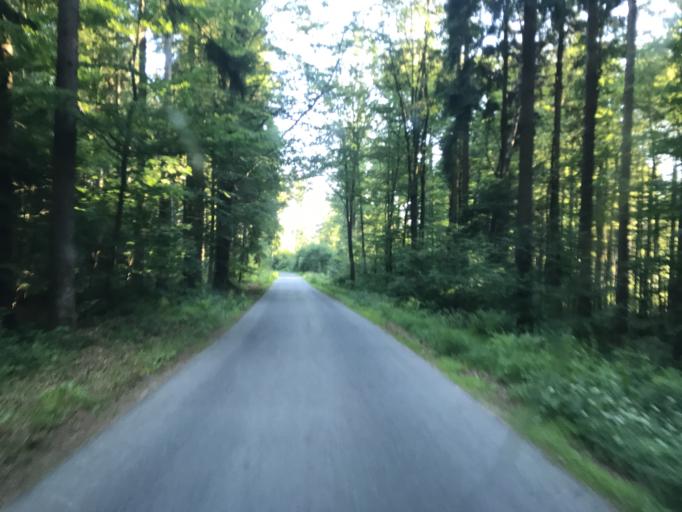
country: DE
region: Bavaria
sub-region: Upper Palatinate
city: Waldmunchen
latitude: 49.3995
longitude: 12.7180
